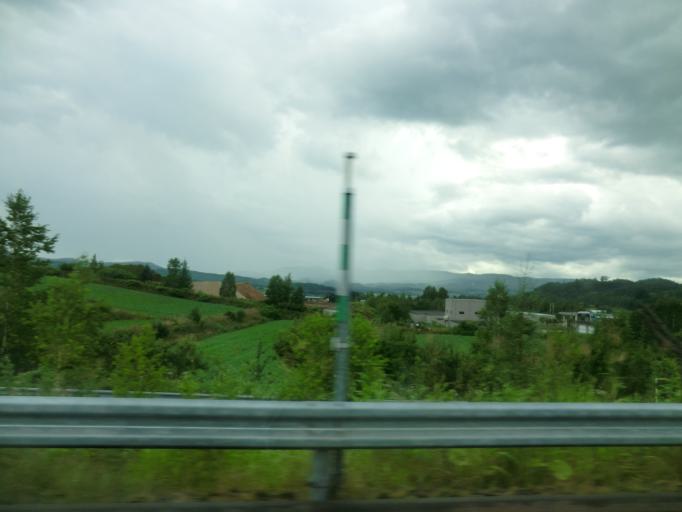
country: JP
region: Hokkaido
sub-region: Asahikawa-shi
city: Asahikawa
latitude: 44.0082
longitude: 142.4370
